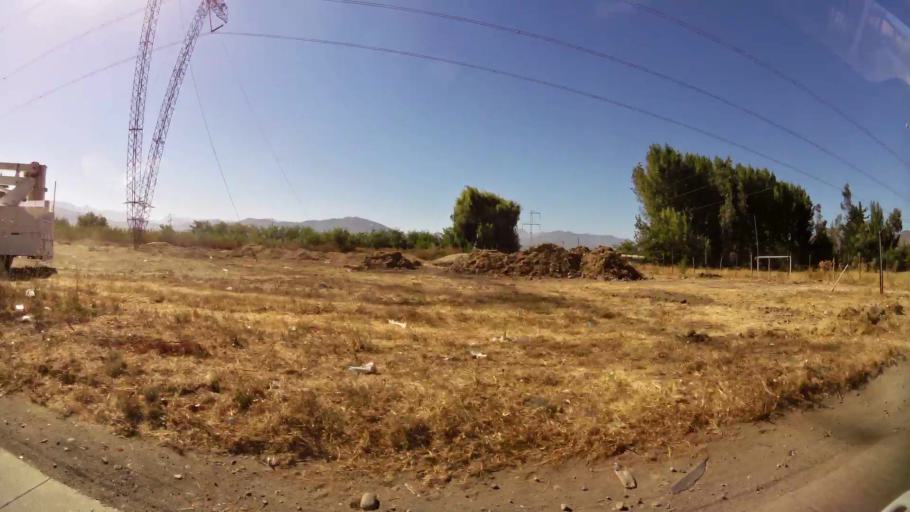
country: CL
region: O'Higgins
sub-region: Provincia de Cachapoal
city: Rancagua
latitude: -34.1811
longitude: -70.7054
